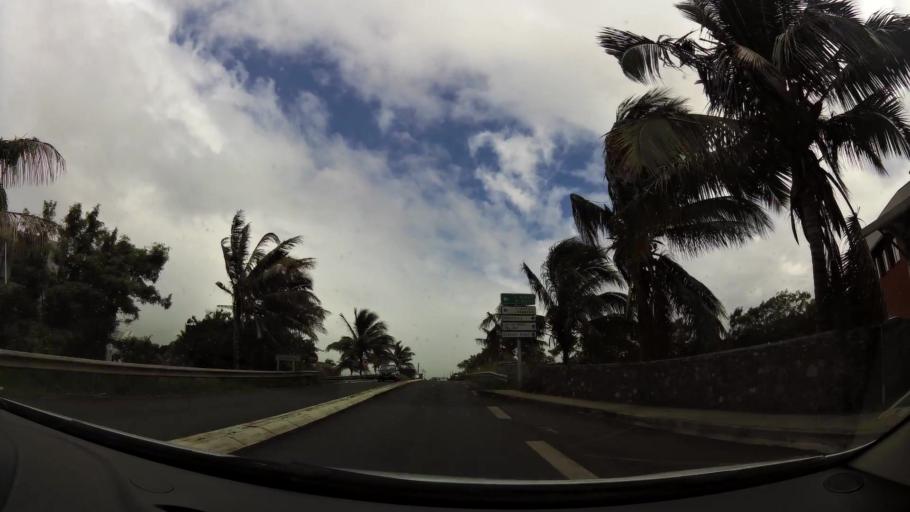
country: RE
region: Reunion
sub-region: Reunion
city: Sainte-Suzanne
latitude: -20.9054
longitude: 55.5999
